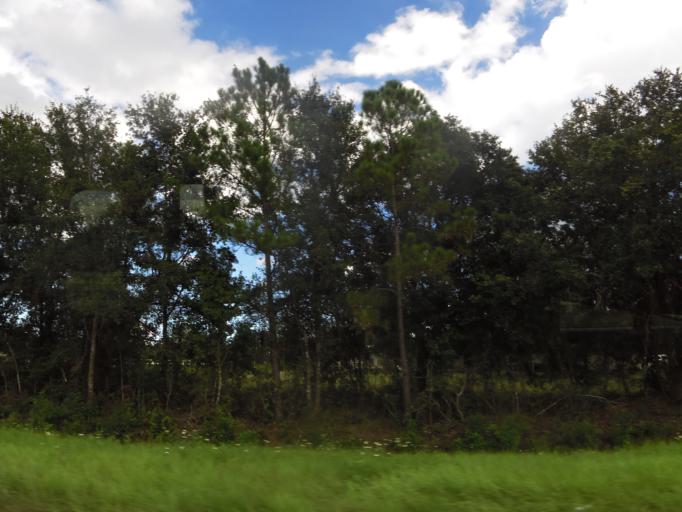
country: US
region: Florida
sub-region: Saint Johns County
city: Saint Augustine
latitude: 29.8937
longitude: -81.4948
